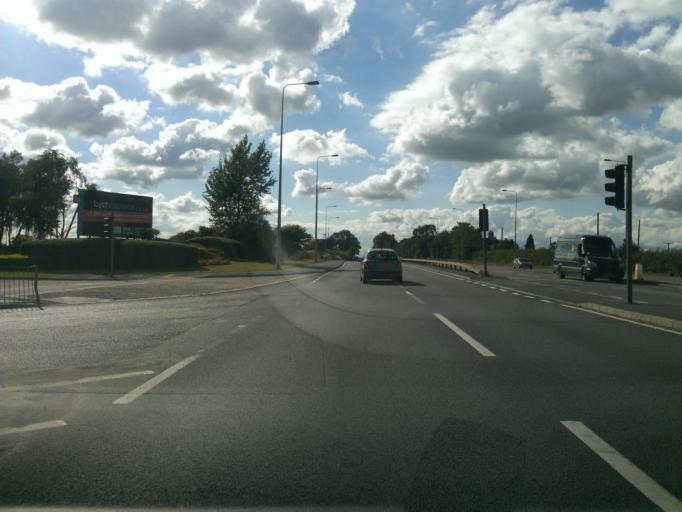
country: GB
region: England
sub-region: Warwickshire
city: Kingsbury
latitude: 52.6007
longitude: -1.6265
